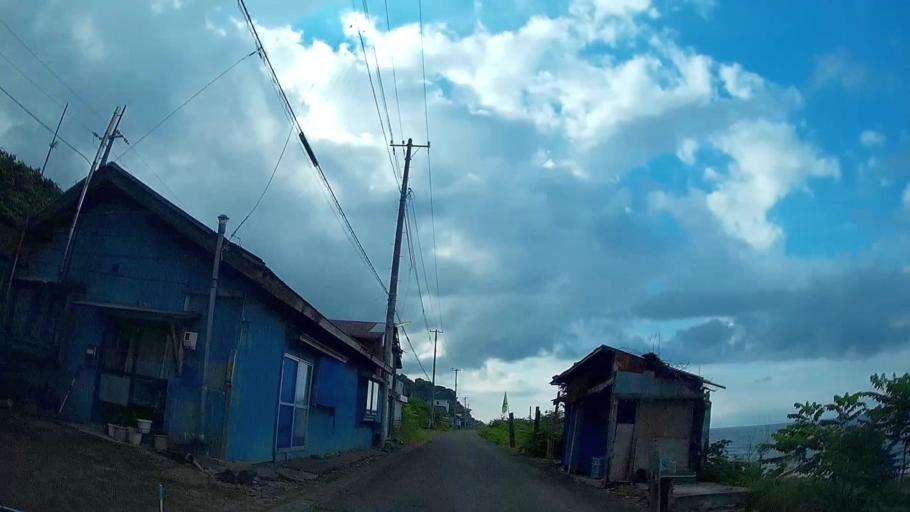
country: JP
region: Hokkaido
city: Nanae
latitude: 42.1164
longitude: 140.5421
